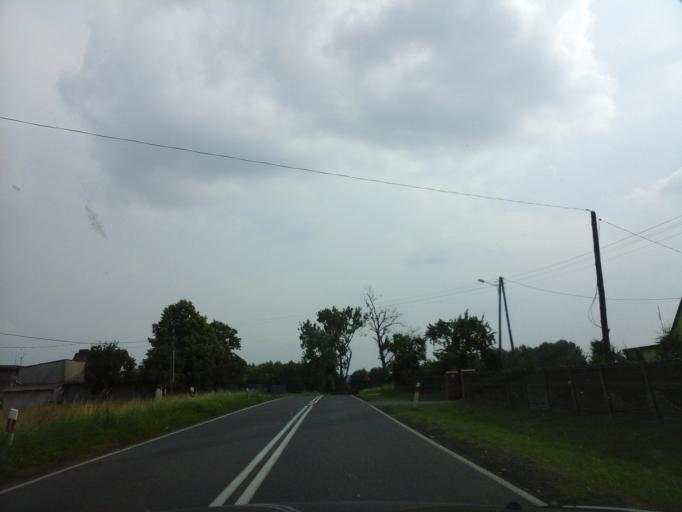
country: PL
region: Lubusz
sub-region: Powiat strzelecko-drezdenecki
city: Dobiegniew
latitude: 52.9870
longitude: 15.7499
